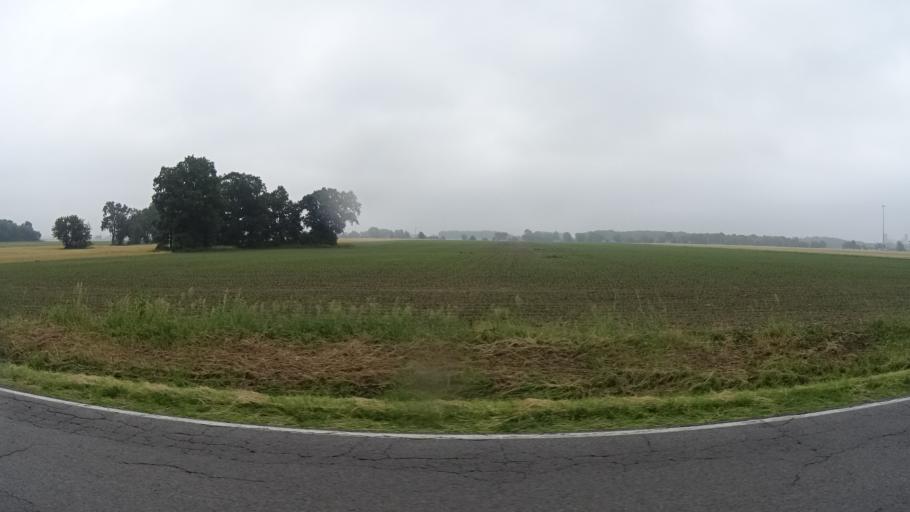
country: US
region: Ohio
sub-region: Huron County
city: Bellevue
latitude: 41.2998
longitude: -82.8419
